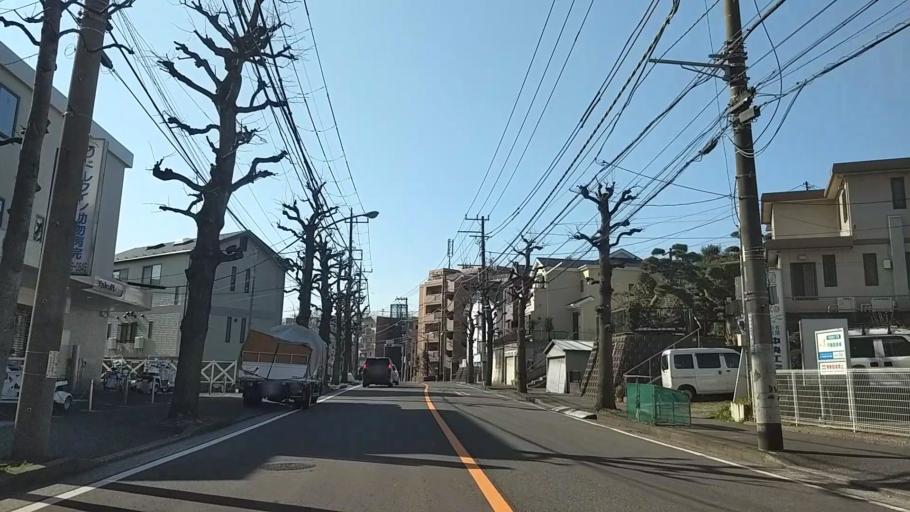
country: JP
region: Kanagawa
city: Yokohama
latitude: 35.3878
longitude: 139.6017
